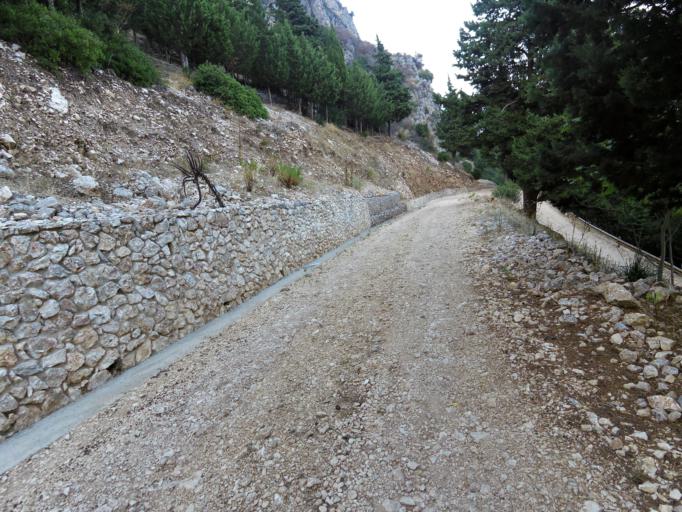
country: IT
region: Calabria
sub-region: Provincia di Reggio Calabria
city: Stilo
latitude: 38.4787
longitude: 16.4643
